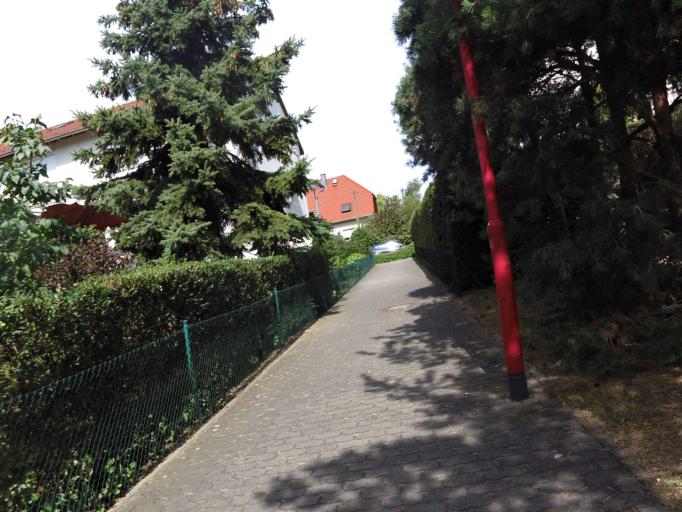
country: DE
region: Saxony
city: Leipzig
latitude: 51.3574
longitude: 12.3000
